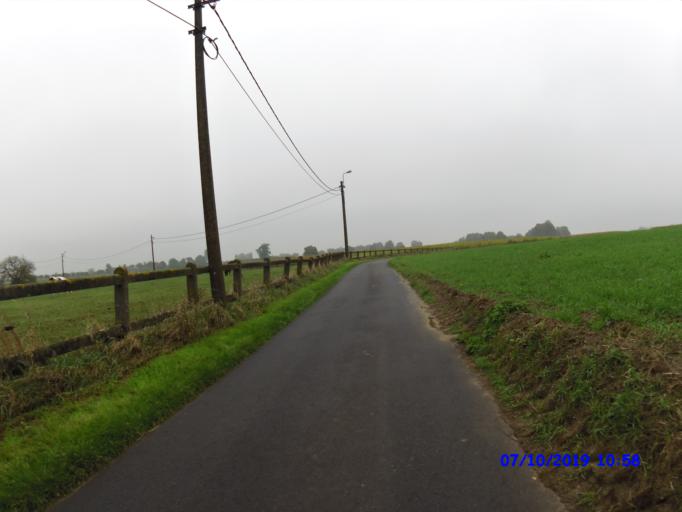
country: BE
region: Flanders
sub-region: Provincie Oost-Vlaanderen
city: Oosterzele
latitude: 50.9760
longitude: 3.7872
